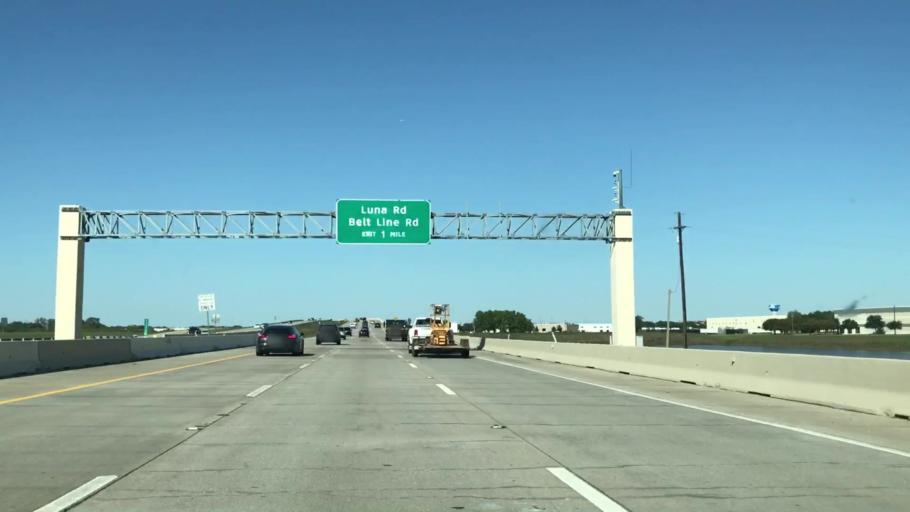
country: US
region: Texas
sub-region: Dallas County
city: Farmers Branch
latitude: 32.9305
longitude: -96.9304
